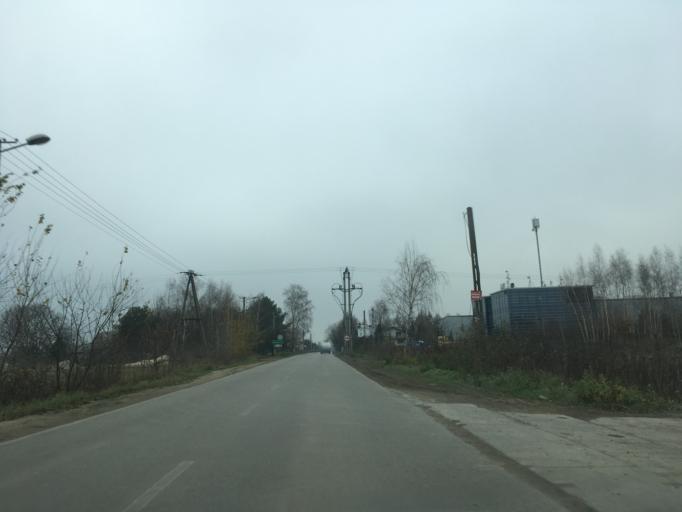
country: PL
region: Masovian Voivodeship
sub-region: Powiat piaseczynski
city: Lesznowola
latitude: 52.0686
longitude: 20.9534
